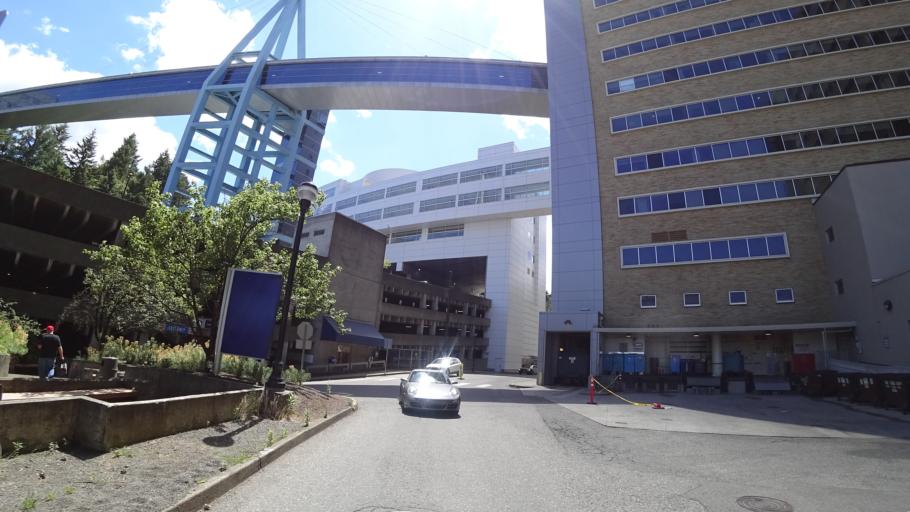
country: US
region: Oregon
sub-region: Multnomah County
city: Portland
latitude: 45.4987
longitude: -122.6852
